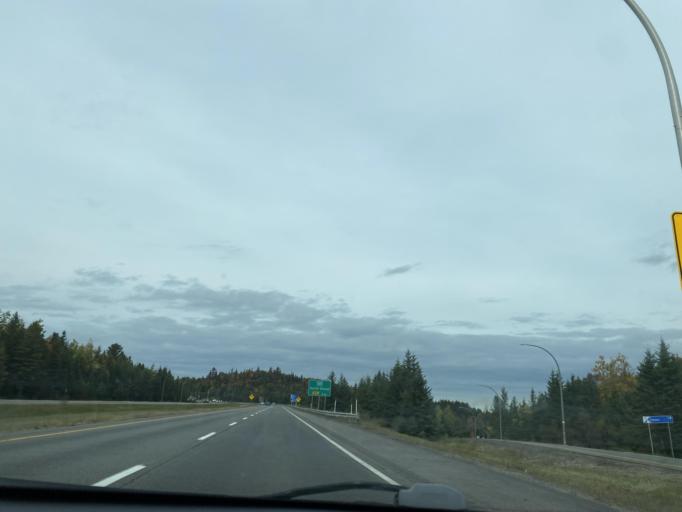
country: CA
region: Quebec
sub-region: Laurentides
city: Sainte-Agathe-des-Monts
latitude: 46.0569
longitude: -74.2731
